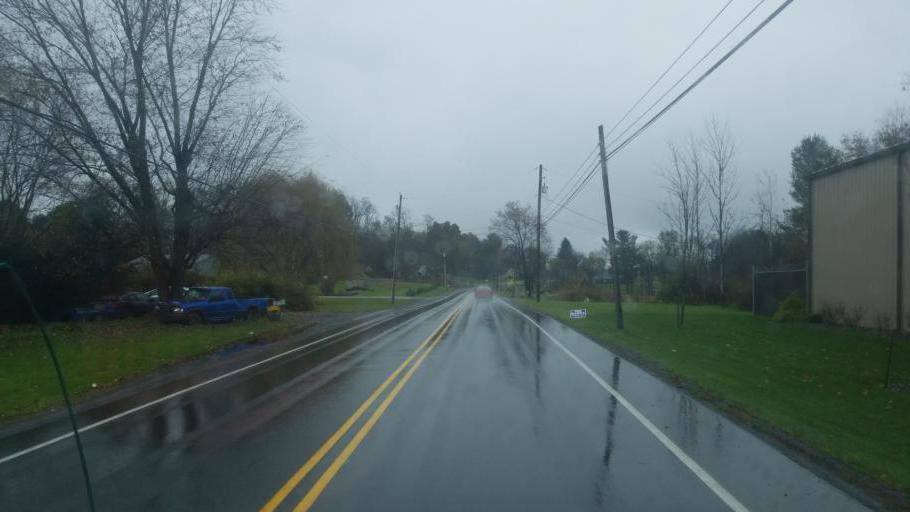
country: US
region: Pennsylvania
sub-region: Clinton County
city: Mill Hall
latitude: 41.1030
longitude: -77.5133
